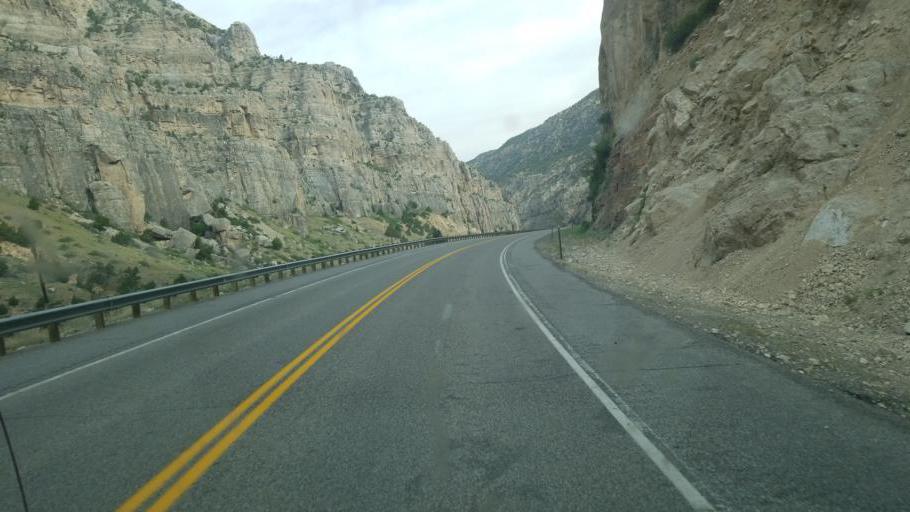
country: US
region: Wyoming
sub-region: Hot Springs County
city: Thermopolis
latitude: 43.5302
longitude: -108.1778
